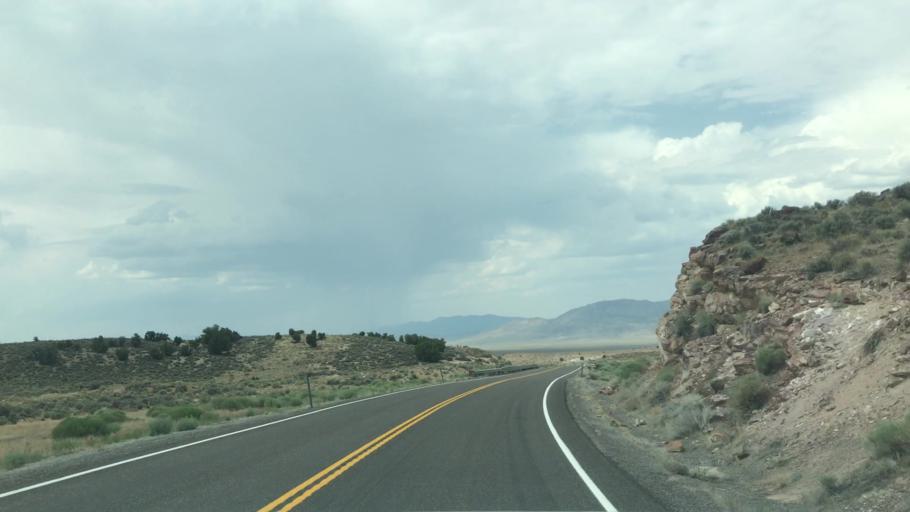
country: US
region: Nevada
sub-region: Eureka County
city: Eureka
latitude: 39.4000
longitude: -115.7066
